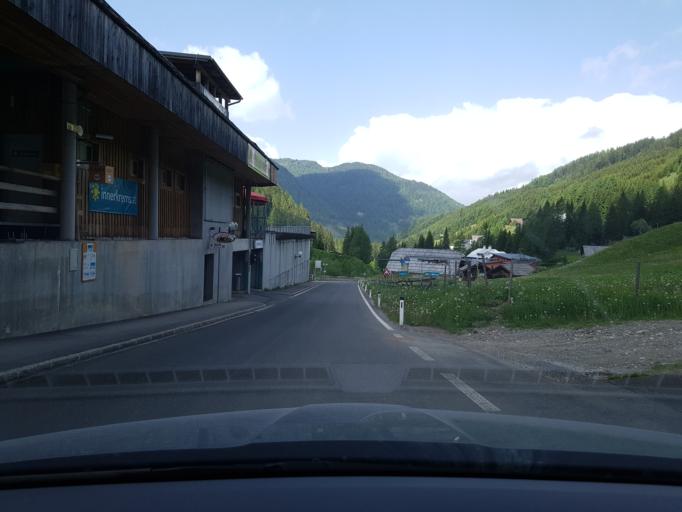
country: AT
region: Salzburg
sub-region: Politischer Bezirk Tamsweg
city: Thomatal
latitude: 46.9714
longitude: 13.7485
